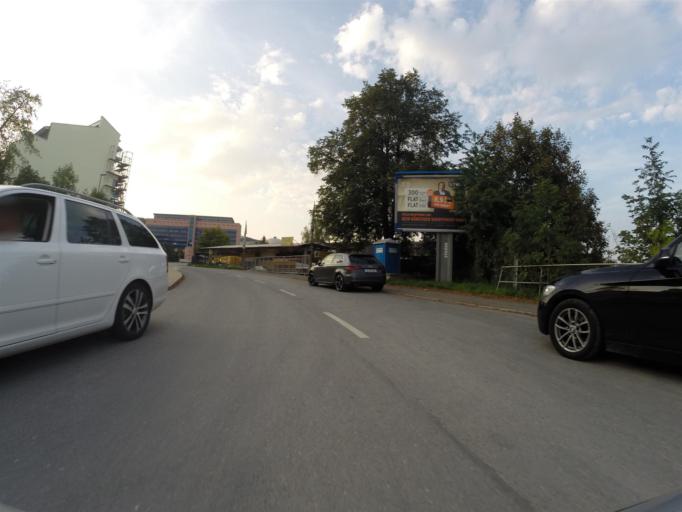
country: DE
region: Thuringia
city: Jena
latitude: 50.9156
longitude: 11.5702
